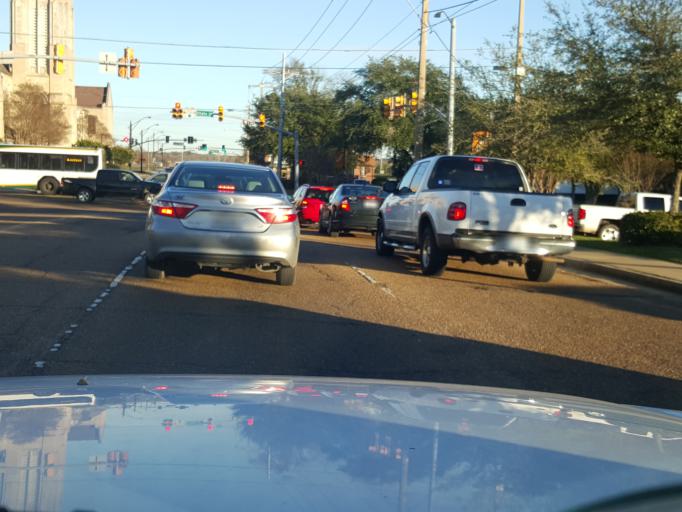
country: US
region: Mississippi
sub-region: Hinds County
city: Jackson
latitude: 32.3046
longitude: -90.1797
